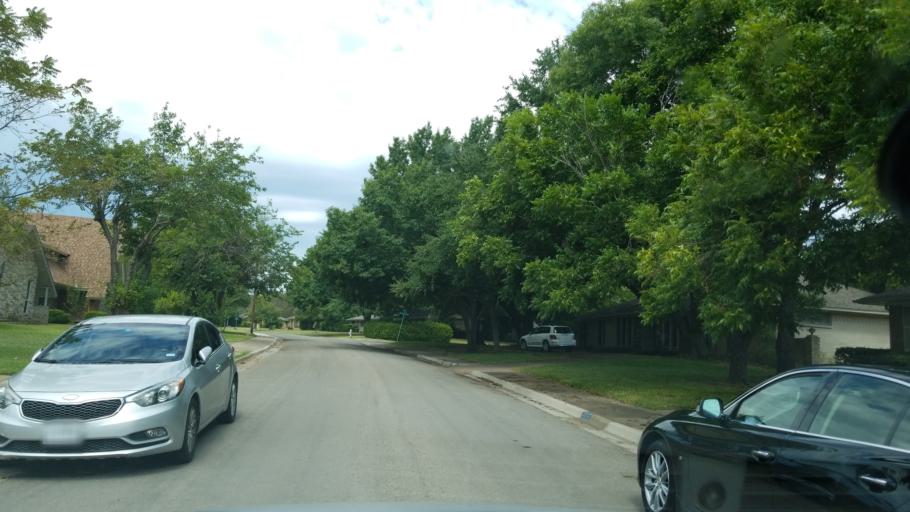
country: US
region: Texas
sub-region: Dallas County
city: Duncanville
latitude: 32.6736
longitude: -96.8516
